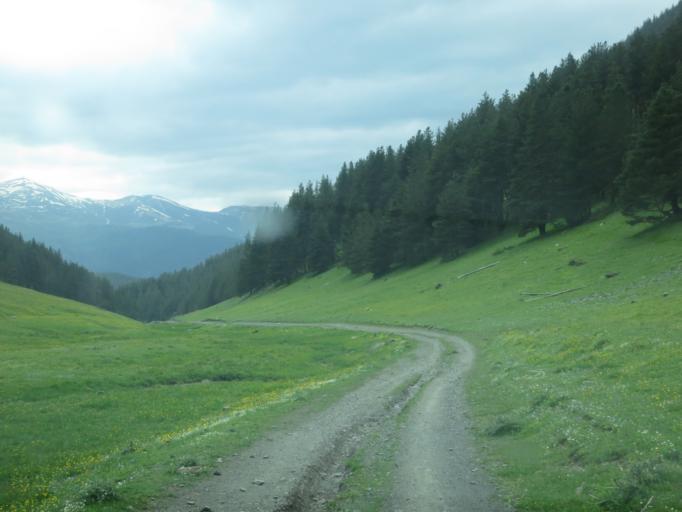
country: RU
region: Chechnya
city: Itum-Kali
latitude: 42.3878
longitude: 45.6746
